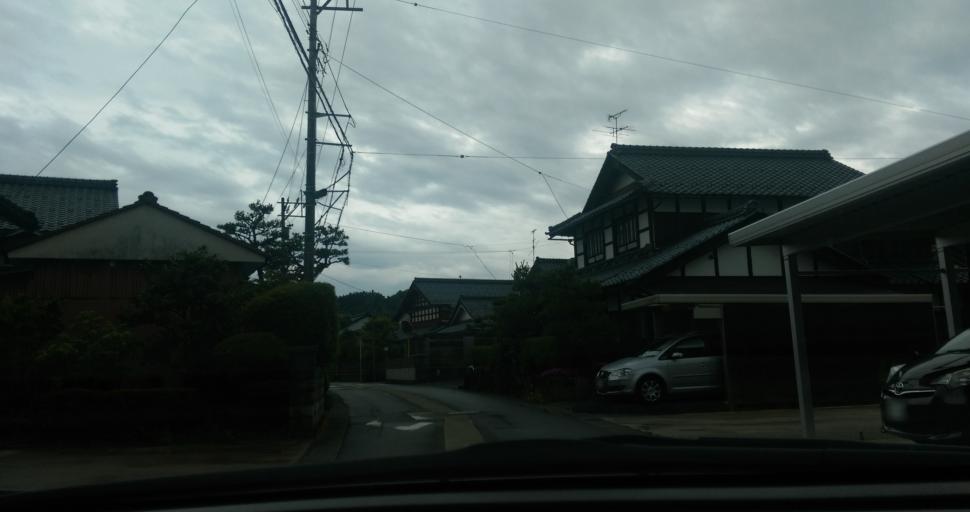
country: JP
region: Fukui
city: Fukui-shi
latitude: 36.0077
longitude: 136.1982
